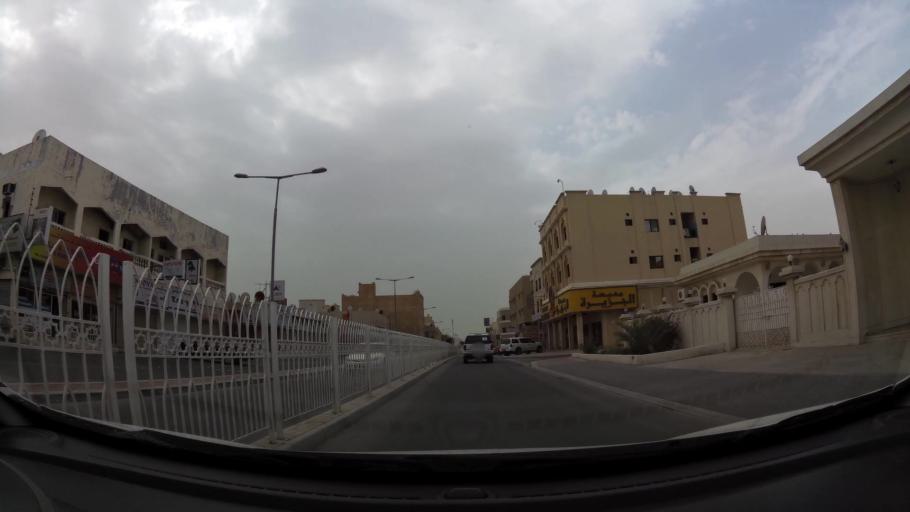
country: BH
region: Northern
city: Ar Rifa'
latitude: 26.1274
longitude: 50.5451
